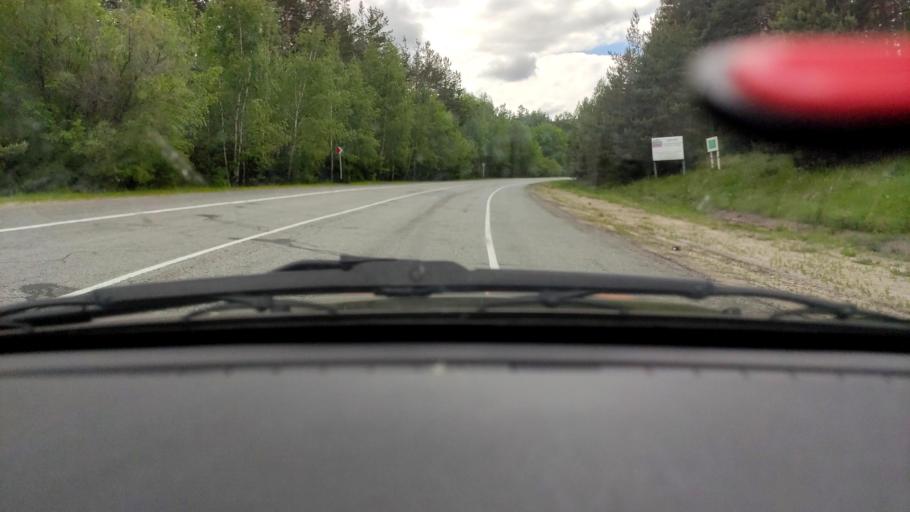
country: RU
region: Belgorod
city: Krasnoye
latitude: 51.0788
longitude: 38.6919
